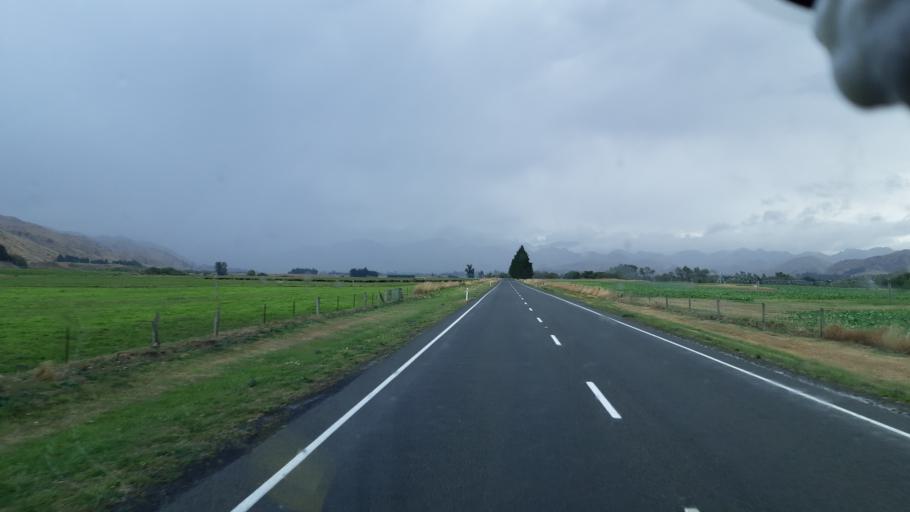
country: NZ
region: Canterbury
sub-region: Hurunui District
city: Amberley
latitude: -42.7106
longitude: 172.8527
